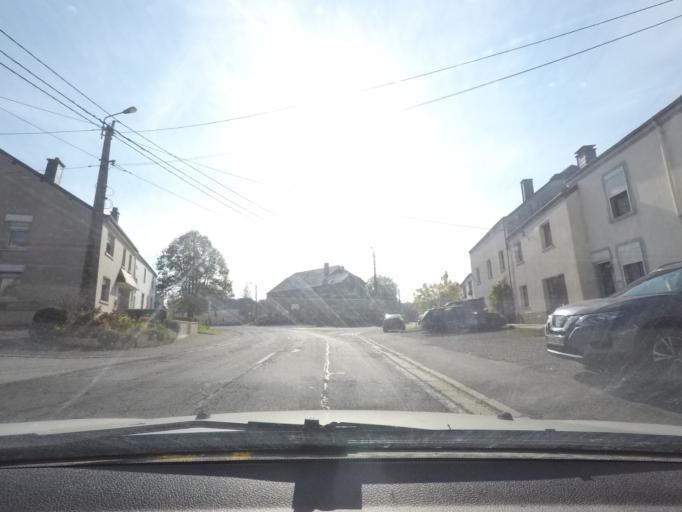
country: BE
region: Wallonia
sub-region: Province du Luxembourg
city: Tintigny
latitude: 49.6951
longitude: 5.4905
